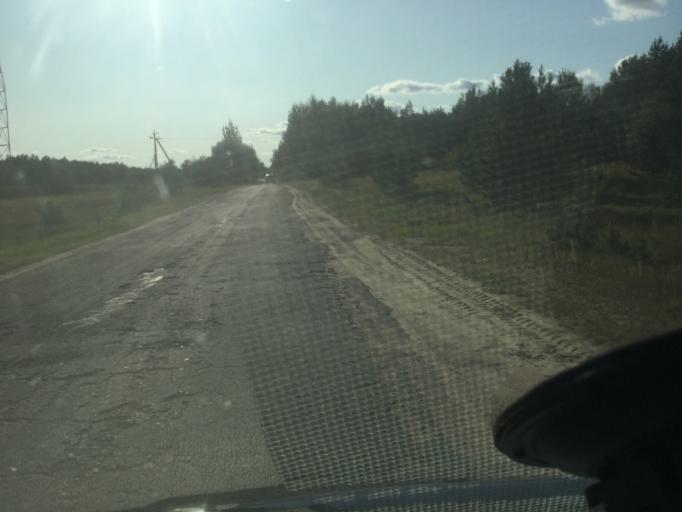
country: BY
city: Osveya
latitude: 56.0217
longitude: 28.2754
